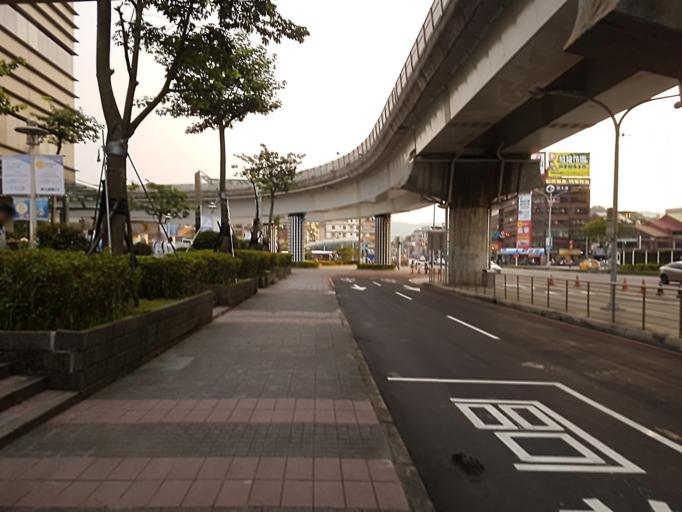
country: TW
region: Taipei
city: Taipei
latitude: 25.0562
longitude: 121.6172
